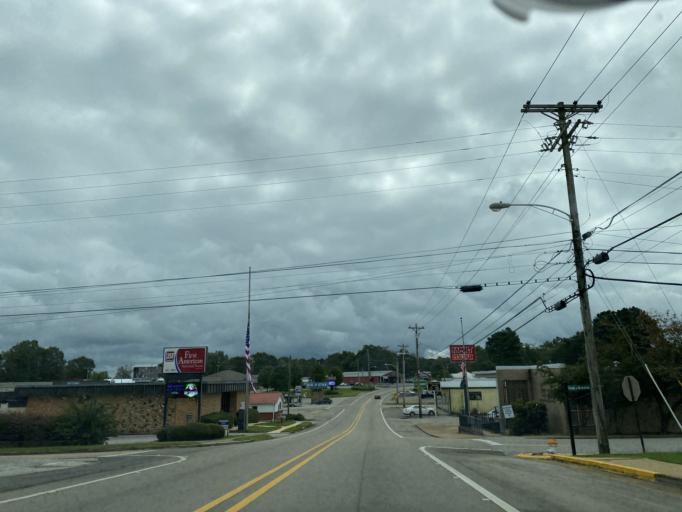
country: US
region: Mississippi
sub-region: Tishomingo County
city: Belmont
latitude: 34.5087
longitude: -88.2084
